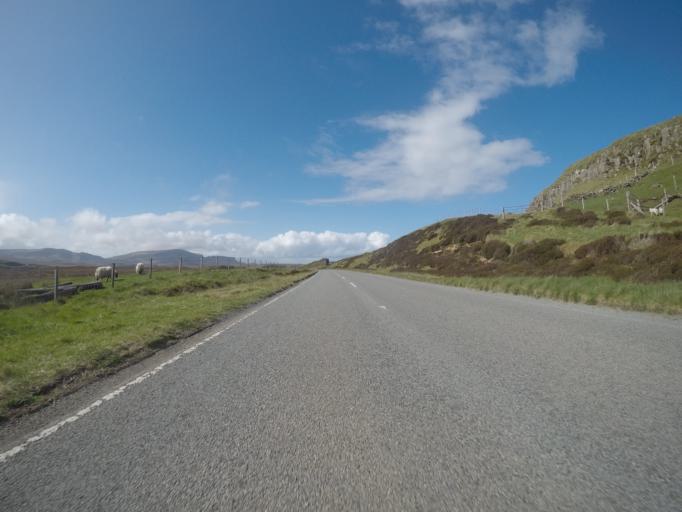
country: GB
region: Scotland
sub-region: Highland
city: Portree
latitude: 57.5996
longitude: -6.1639
